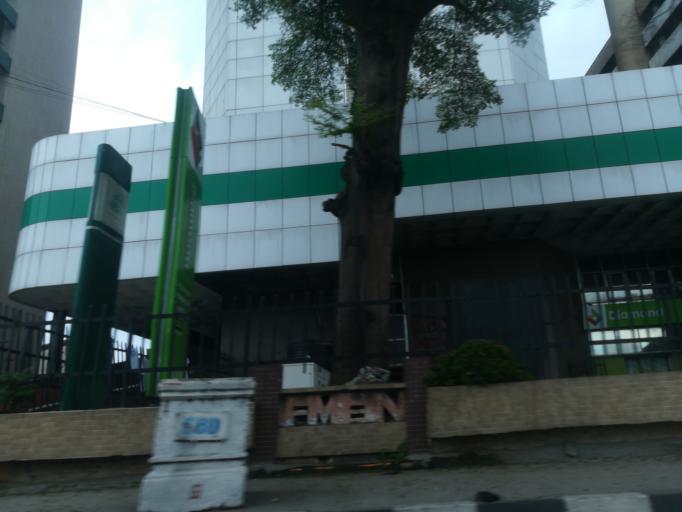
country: NG
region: Lagos
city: Lagos
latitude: 6.4495
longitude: 3.3914
